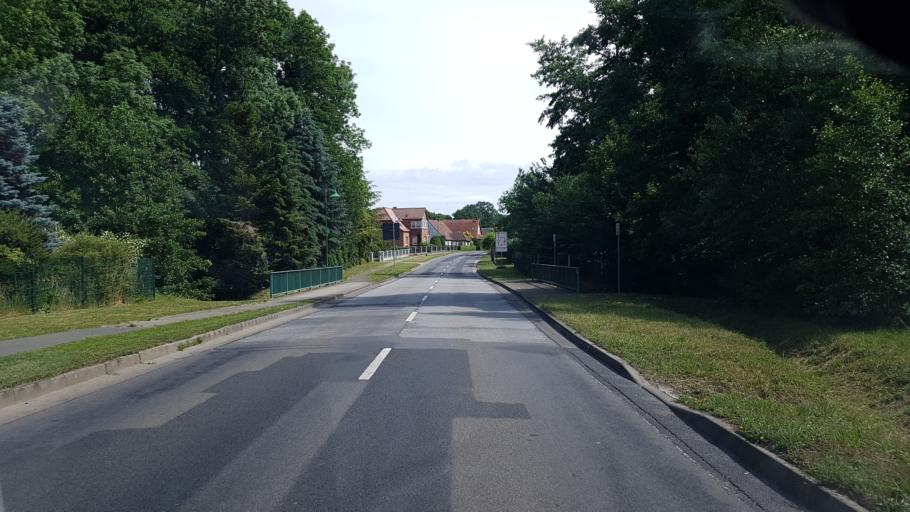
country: DE
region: Brandenburg
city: Prenzlau
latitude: 53.3640
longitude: 13.7952
